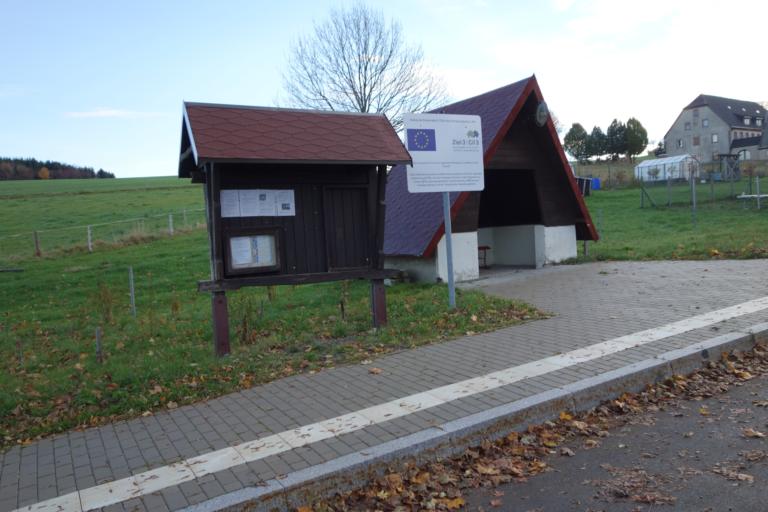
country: DE
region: Saxony
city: Rechenberg-Bienenmuhle
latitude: 50.7316
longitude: 13.5101
